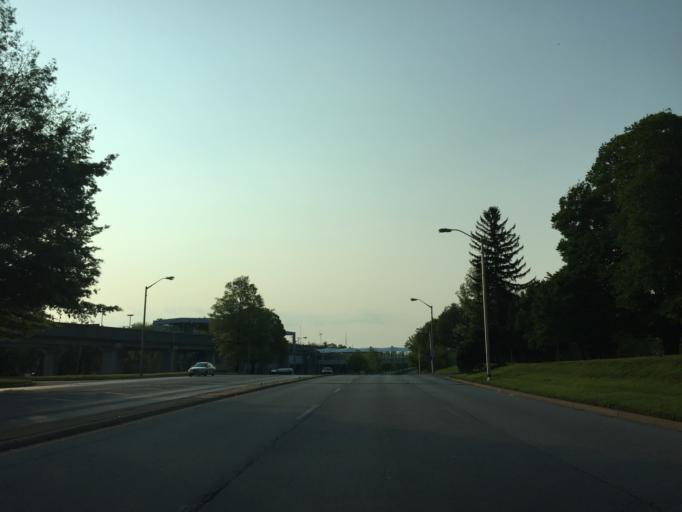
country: US
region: Maryland
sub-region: Baltimore County
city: Lochearn
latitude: 39.3523
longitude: -76.7067
